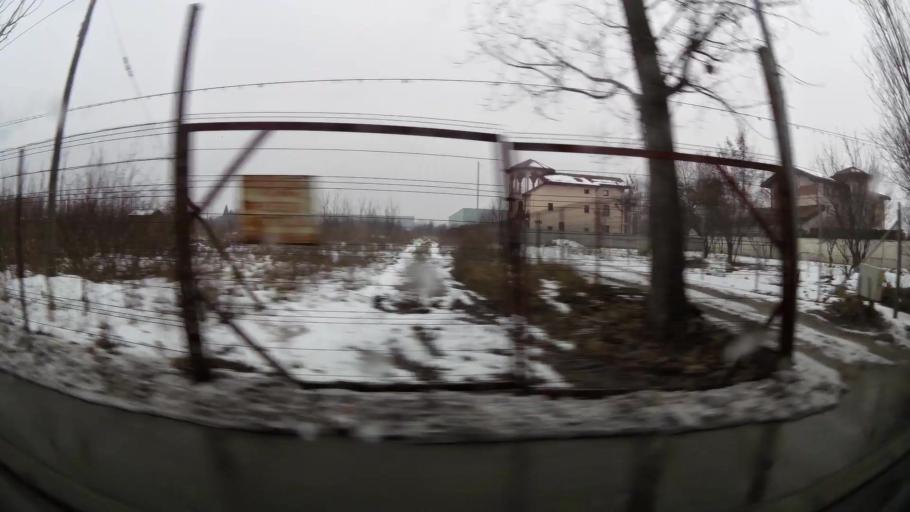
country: RO
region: Ilfov
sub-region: Comuna Otopeni
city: Otopeni
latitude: 44.4870
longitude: 26.0662
